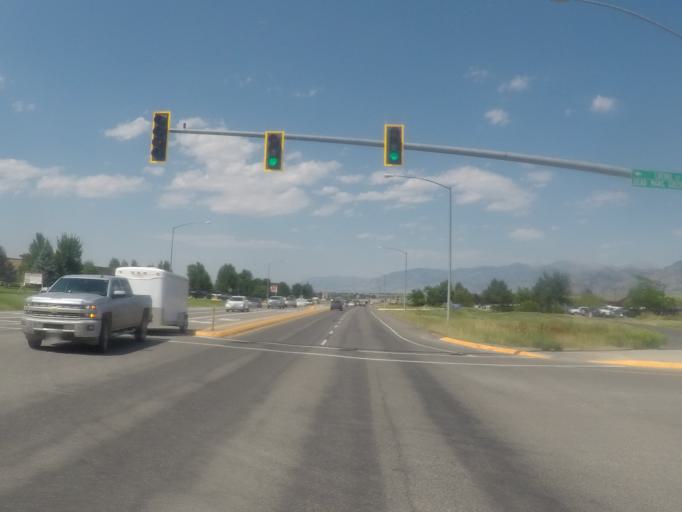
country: US
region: Montana
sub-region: Gallatin County
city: Bozeman
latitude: 45.7076
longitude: -111.0655
